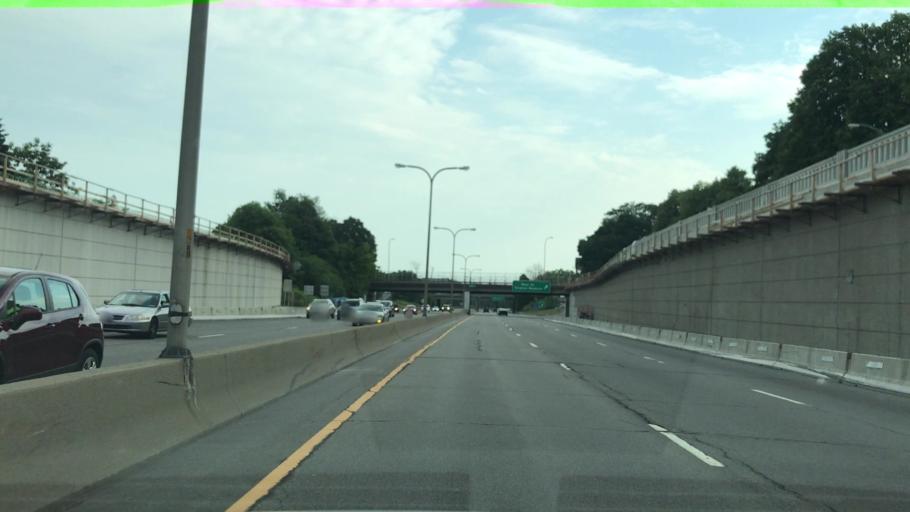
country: US
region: New York
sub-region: Erie County
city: Buffalo
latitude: 42.9068
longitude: -78.8442
